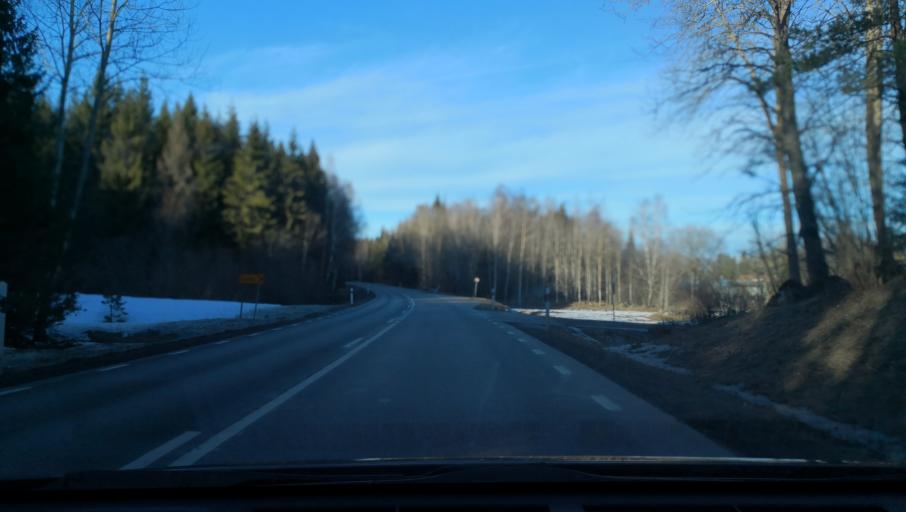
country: SE
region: Uppsala
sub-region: Osthammars Kommun
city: Gimo
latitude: 60.2012
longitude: 18.1941
